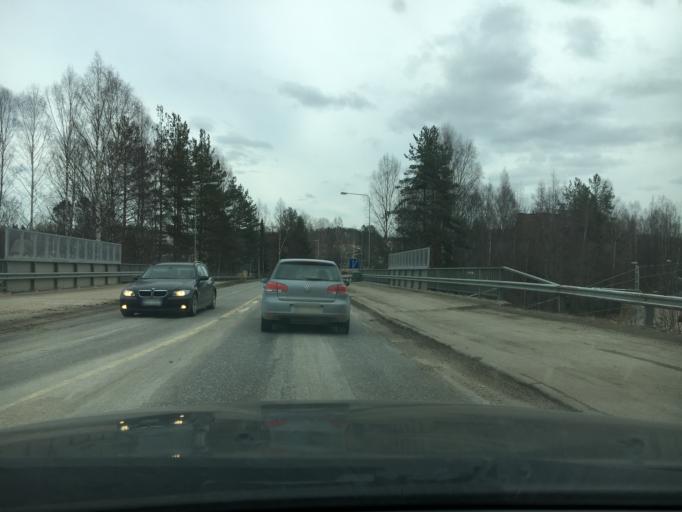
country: FI
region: Central Finland
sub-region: AEaenekoski
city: Suolahti
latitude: 62.5637
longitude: 25.8426
